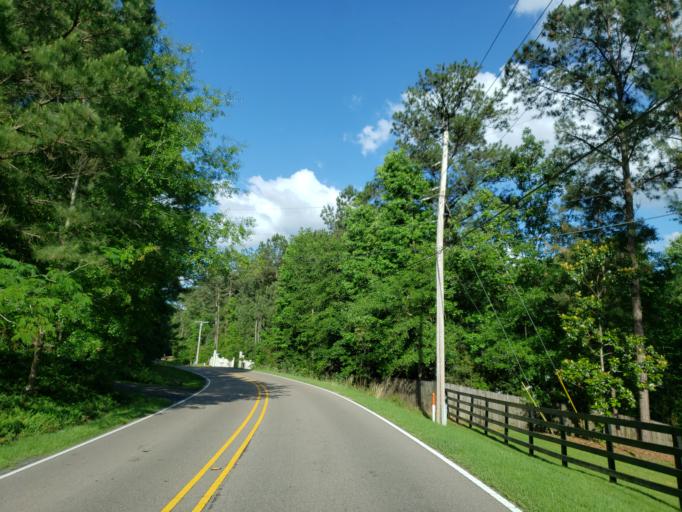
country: US
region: Mississippi
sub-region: Lamar County
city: West Hattiesburg
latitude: 31.2721
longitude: -89.4053
